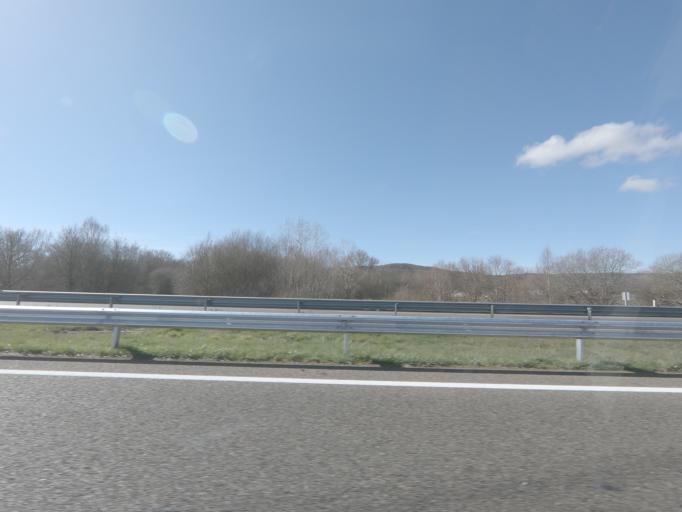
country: ES
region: Galicia
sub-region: Provincia de Ourense
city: Xinzo de Limia
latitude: 42.1300
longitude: -7.7412
